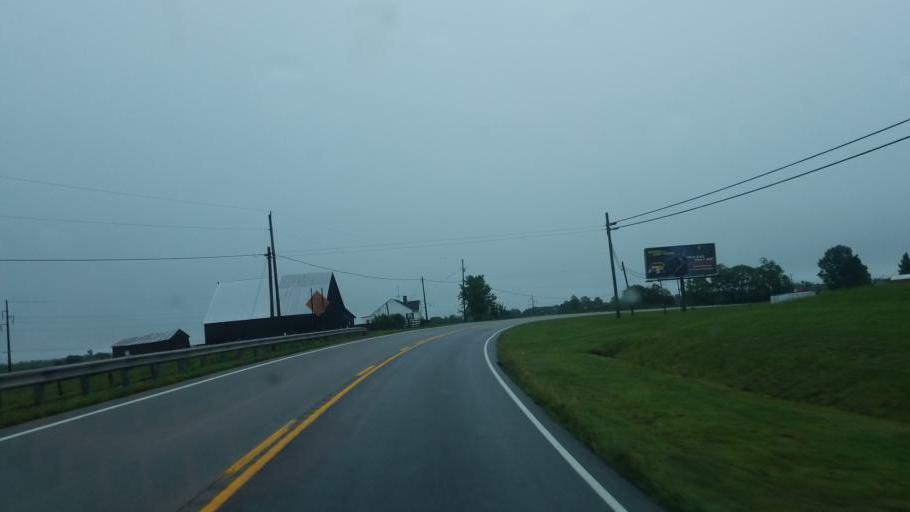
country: US
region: Kentucky
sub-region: Fleming County
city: Flemingsburg
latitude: 38.3974
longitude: -83.6993
